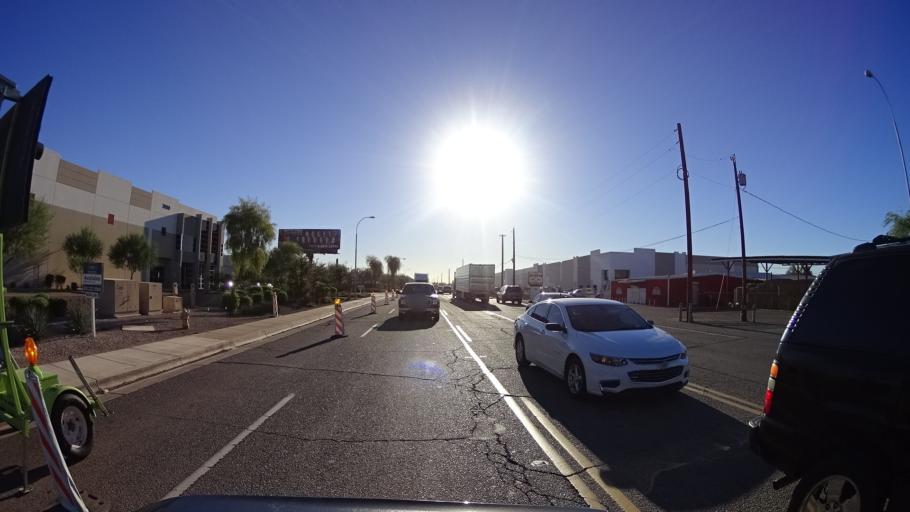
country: US
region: Arizona
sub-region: Maricopa County
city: Tolleson
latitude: 33.4372
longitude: -112.2175
